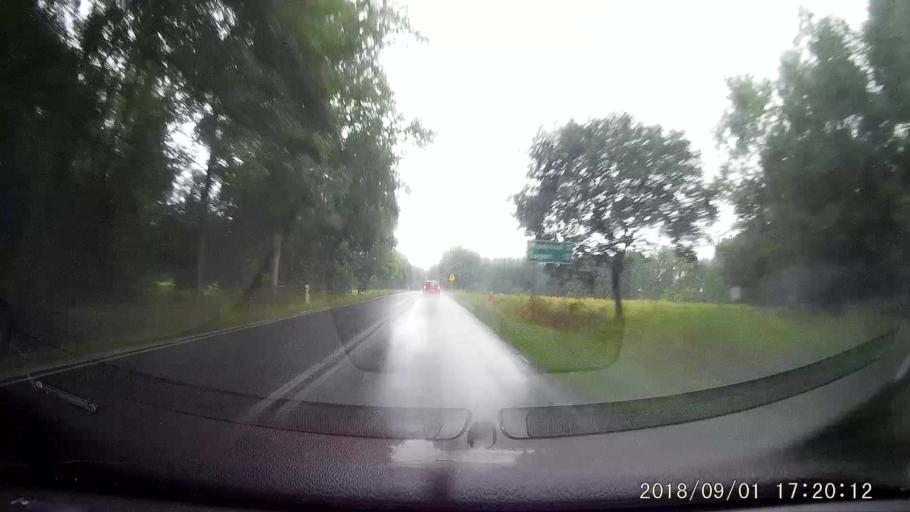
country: PL
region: Lubusz
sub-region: Powiat zielonogorski
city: Nowogrod Bobrzanski
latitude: 51.7268
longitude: 15.2774
